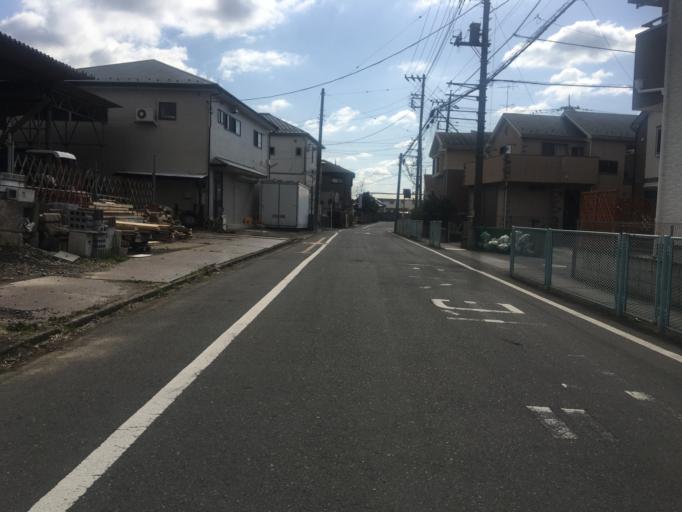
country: JP
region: Saitama
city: Shiki
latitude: 35.8706
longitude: 139.5939
